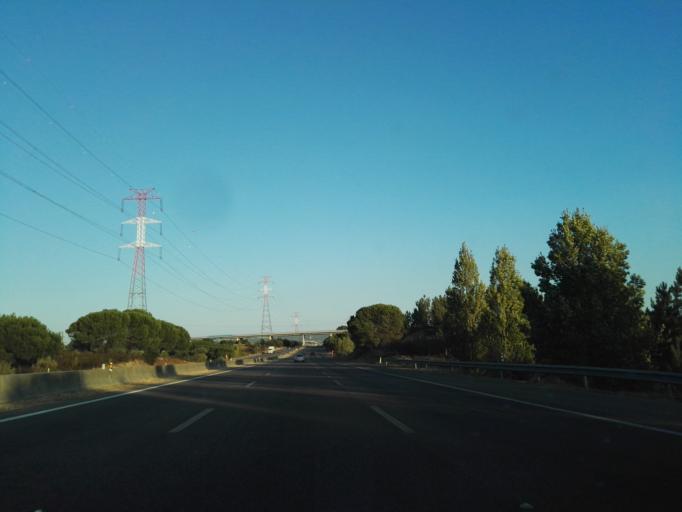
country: PT
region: Setubal
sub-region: Seixal
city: Aldeia de Paio Pires
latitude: 38.5921
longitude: -9.0670
